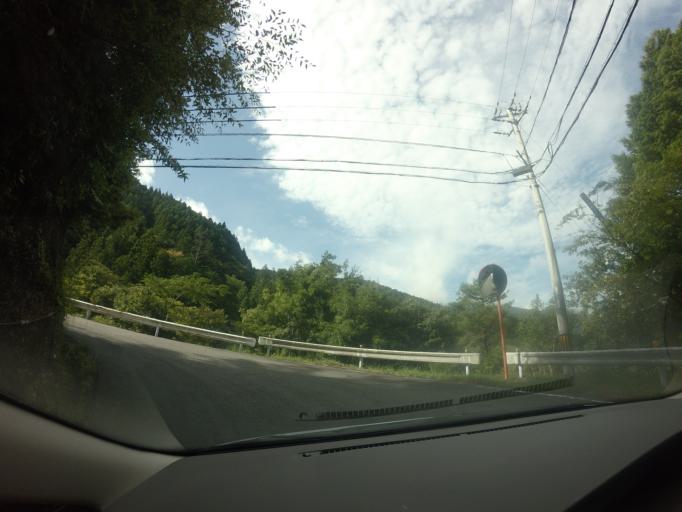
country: JP
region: Wakayama
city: Shingu
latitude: 33.9661
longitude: 135.8488
